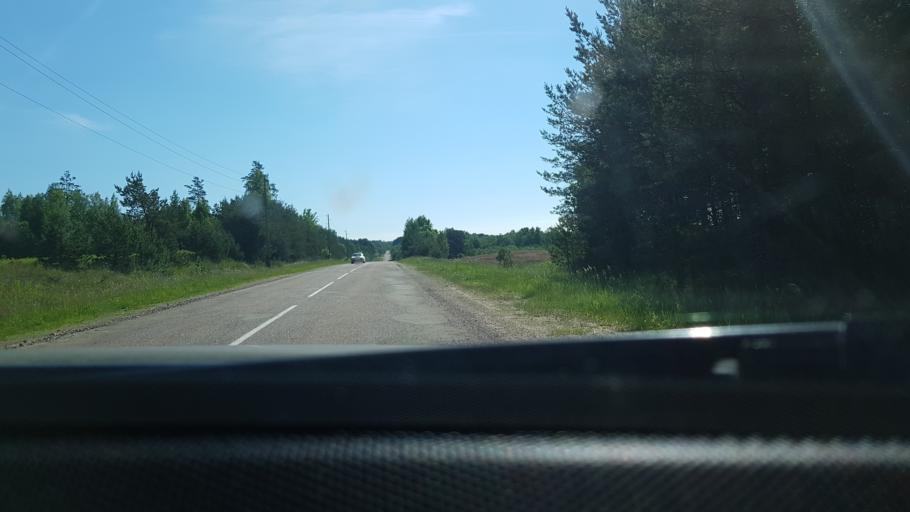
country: LV
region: Kraslavas Rajons
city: Kraslava
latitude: 55.8633
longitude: 26.9898
